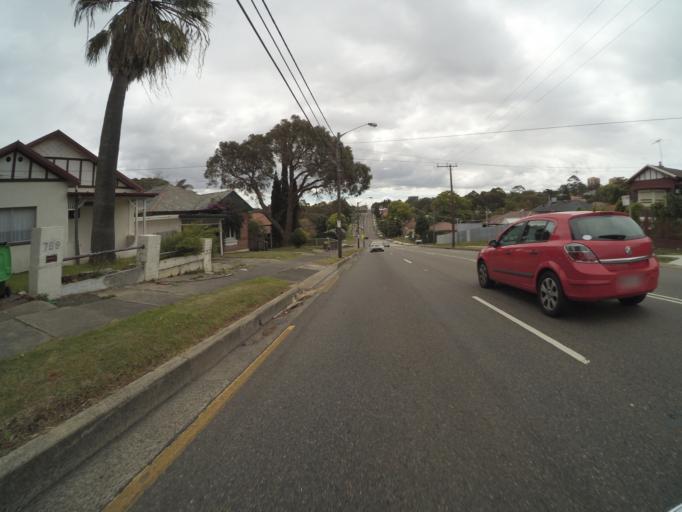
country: AU
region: New South Wales
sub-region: Kogarah
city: Hurstville Grove
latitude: -33.9746
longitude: 151.1022
